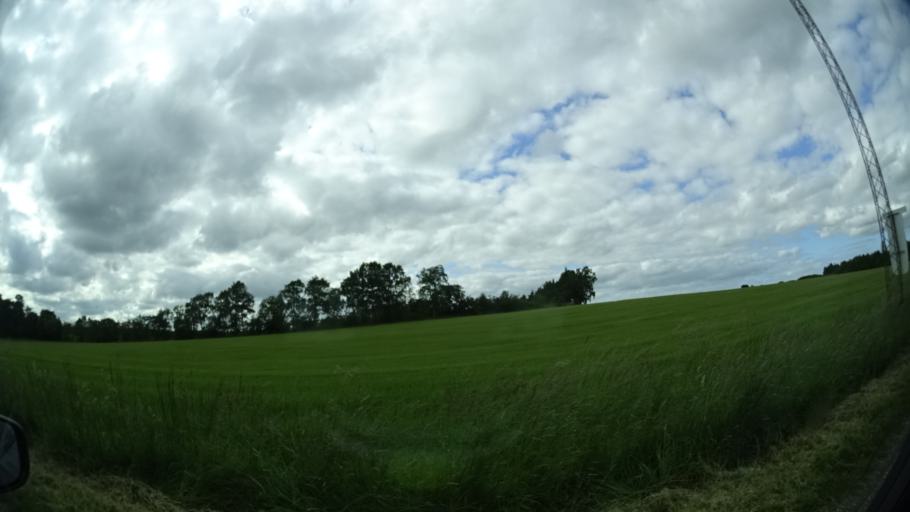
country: DK
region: Central Jutland
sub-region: Syddjurs Kommune
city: Ryomgard
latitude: 56.4111
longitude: 10.5739
